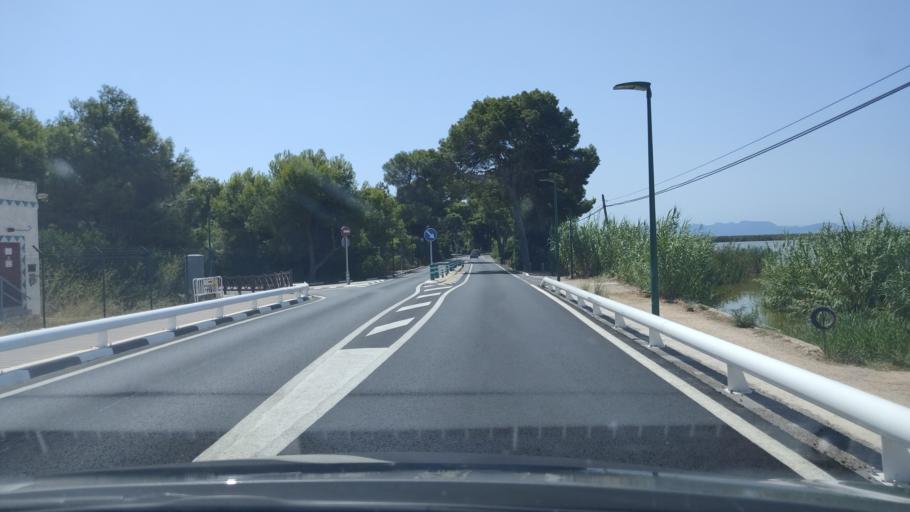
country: ES
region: Valencia
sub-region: Provincia de Valencia
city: Sollana
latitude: 39.3480
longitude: -0.3230
